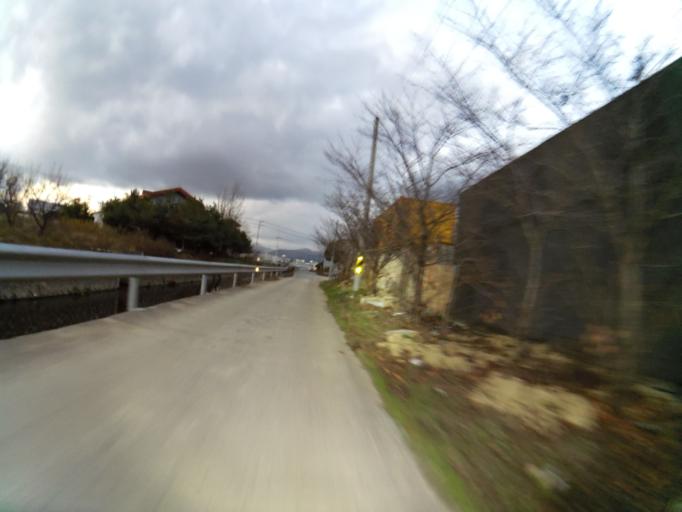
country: KR
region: Gyeongsangbuk-do
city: Gyeongsan-si
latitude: 35.8443
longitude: 128.7449
